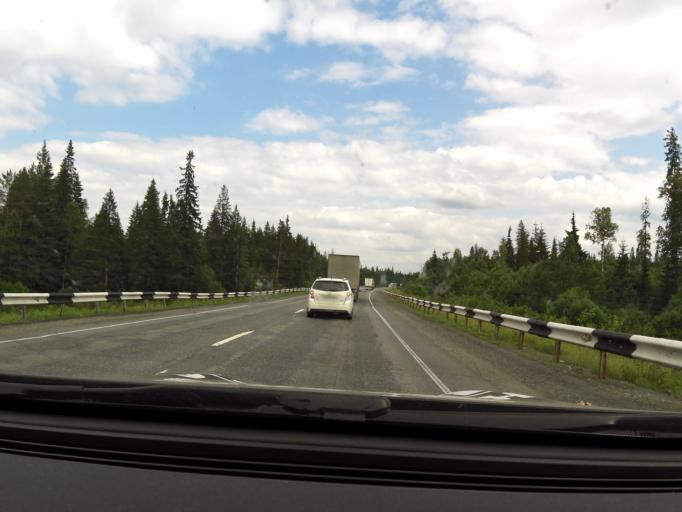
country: RU
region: Sverdlovsk
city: Atig
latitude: 56.8216
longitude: 59.3365
